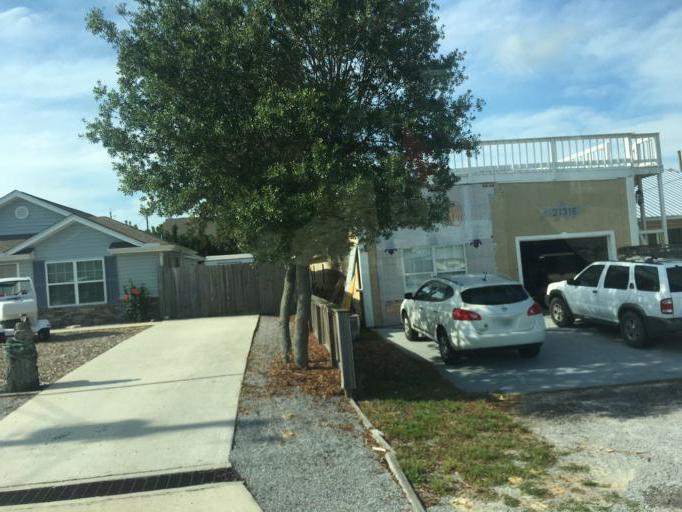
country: US
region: Florida
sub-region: Bay County
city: Laguna Beach
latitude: 30.2558
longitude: -85.9507
